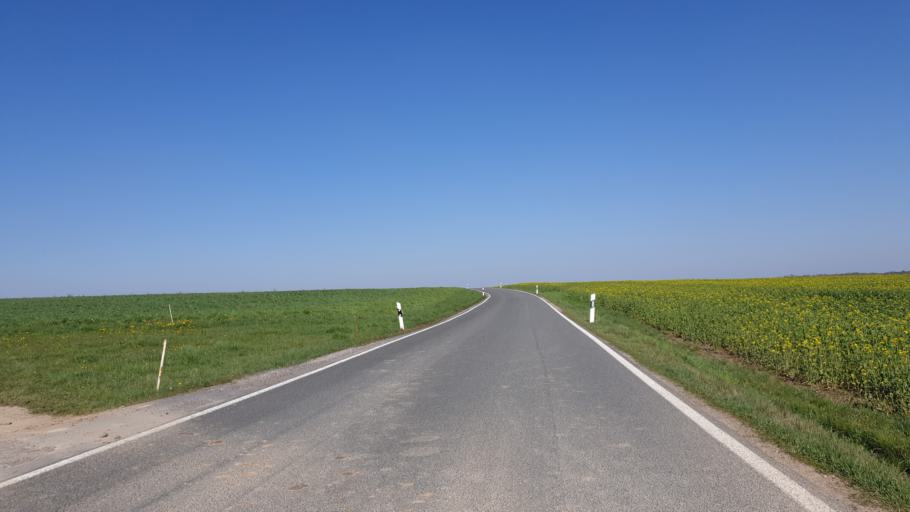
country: DE
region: Saxony
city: Taura
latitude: 50.9234
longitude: 12.8353
